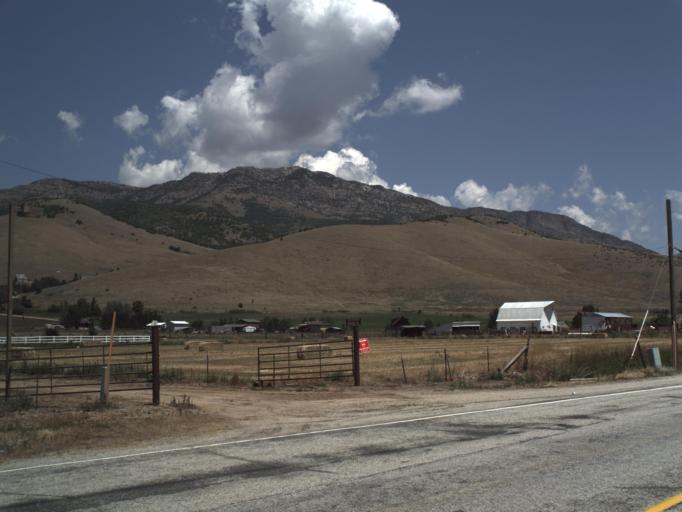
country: US
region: Utah
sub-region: Weber County
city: Wolf Creek
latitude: 41.2620
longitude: -111.7403
